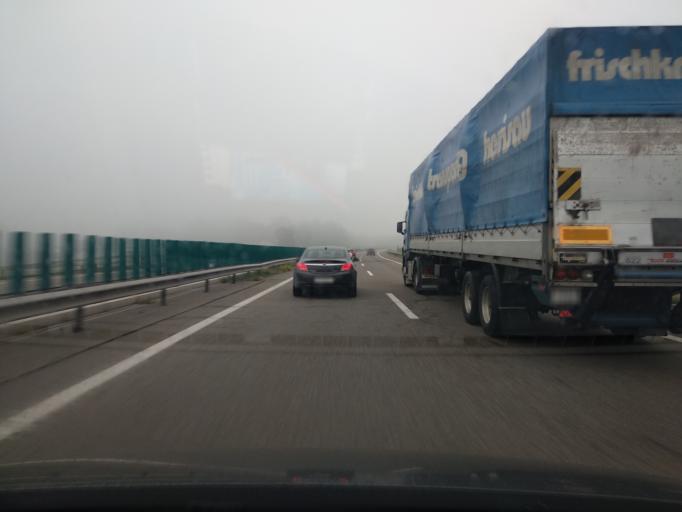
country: CH
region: Saint Gallen
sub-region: Wahlkreis Wil
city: Flawil
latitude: 47.4311
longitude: 9.2086
